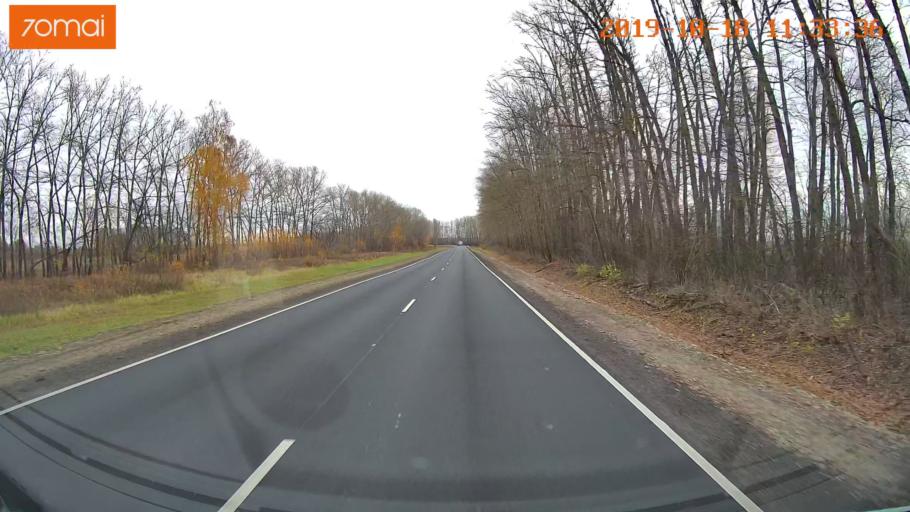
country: RU
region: Rjazan
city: Oktyabr'skiy
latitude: 54.1397
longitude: 38.7443
